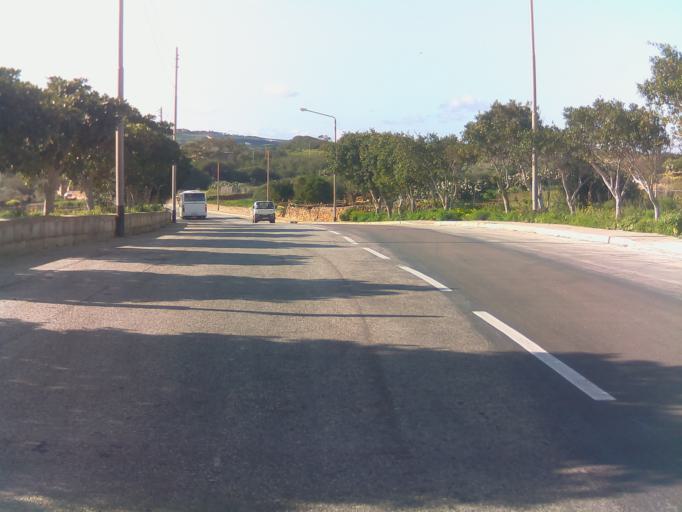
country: MT
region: L-Imgarr
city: Imgarr
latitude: 35.9268
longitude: 14.3689
